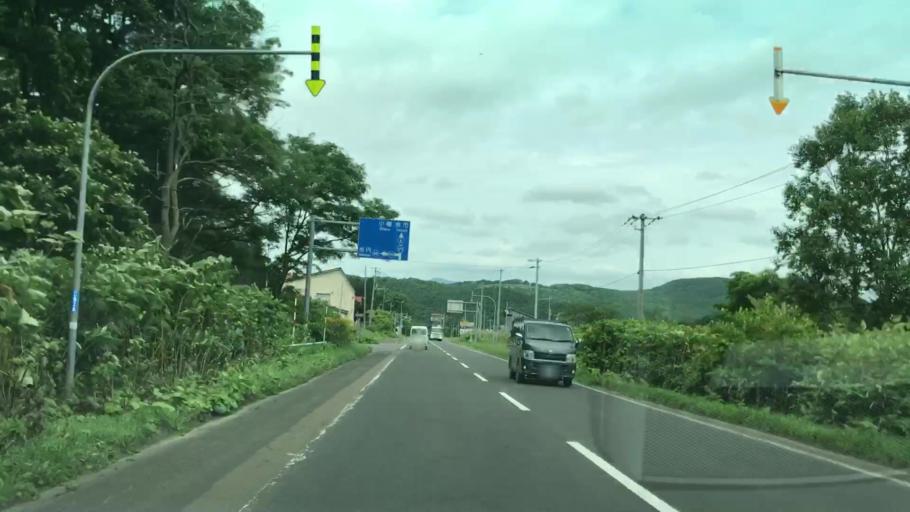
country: JP
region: Hokkaido
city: Niseko Town
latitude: 42.9572
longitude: 140.6957
